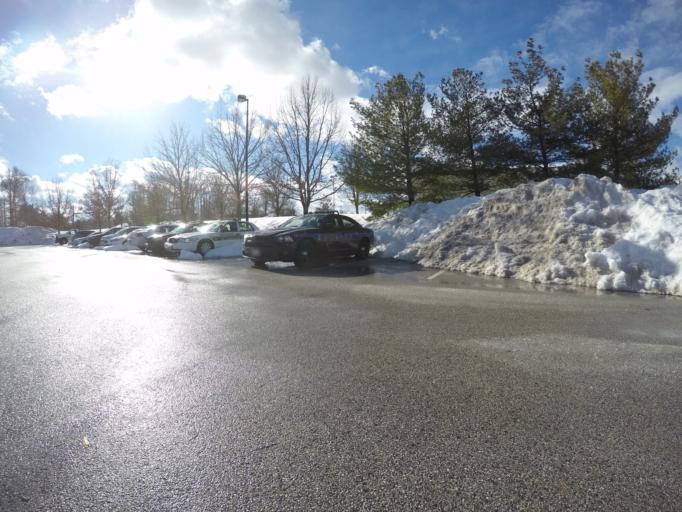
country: US
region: Maryland
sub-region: Anne Arundel County
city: Jessup
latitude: 39.1844
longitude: -76.8024
